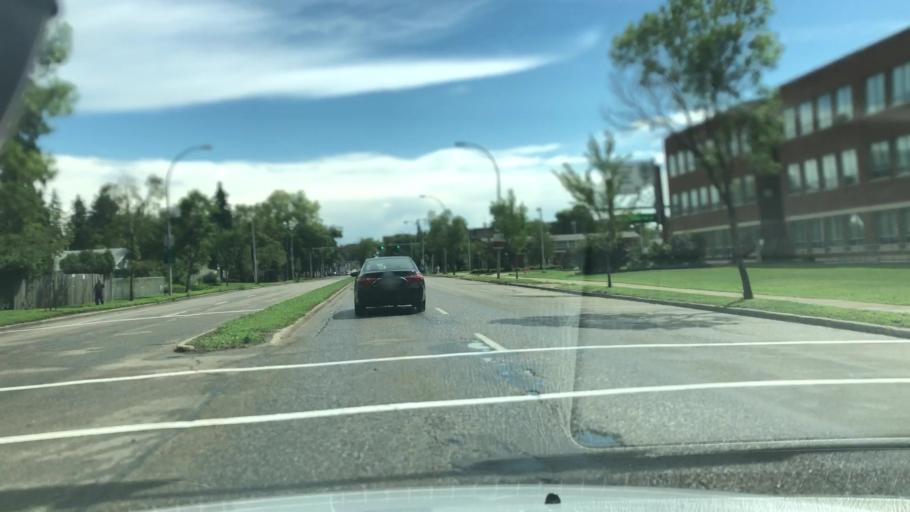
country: CA
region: Alberta
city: Edmonton
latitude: 53.5546
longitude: -113.5085
